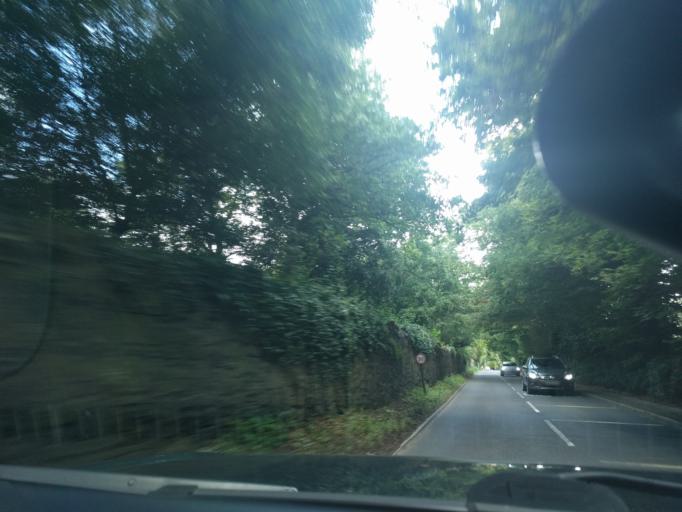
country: GB
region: England
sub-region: Bath and North East Somerset
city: Freshford
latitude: 51.3641
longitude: -2.3184
